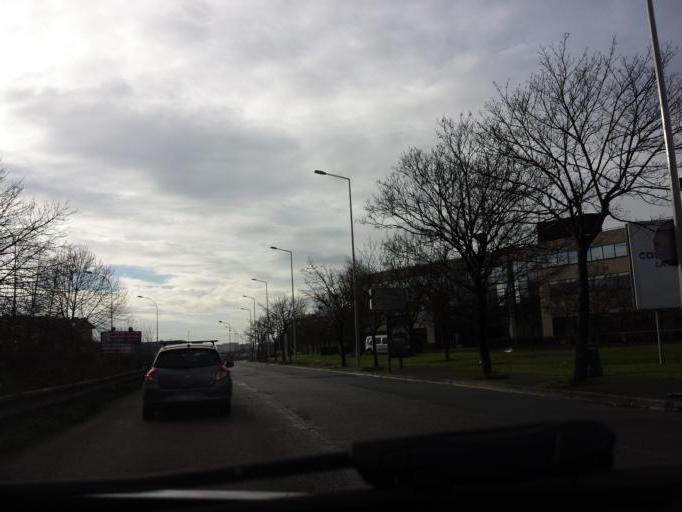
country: FR
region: Ile-de-France
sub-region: Departement du Val-d'Oise
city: Bezons
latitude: 48.9176
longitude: 2.2218
